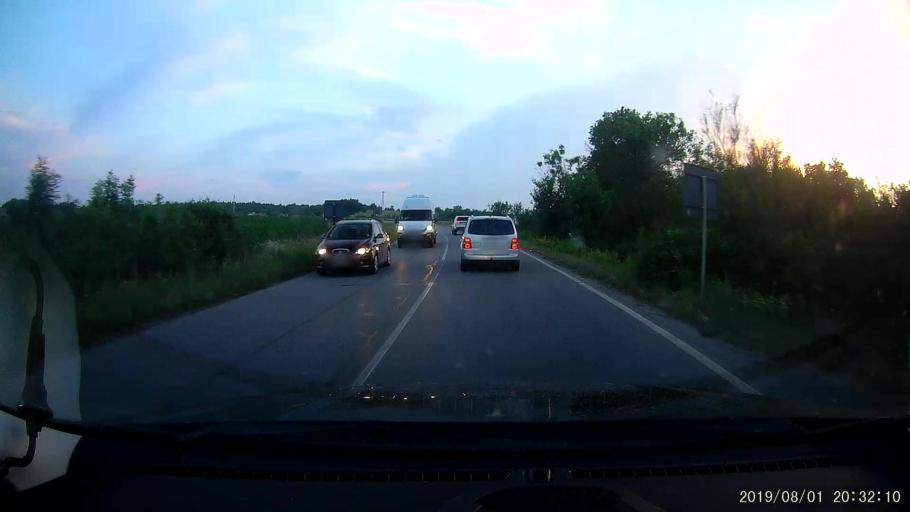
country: BG
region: Yambol
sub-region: Obshtina Elkhovo
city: Elkhovo
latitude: 42.1244
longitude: 26.5329
